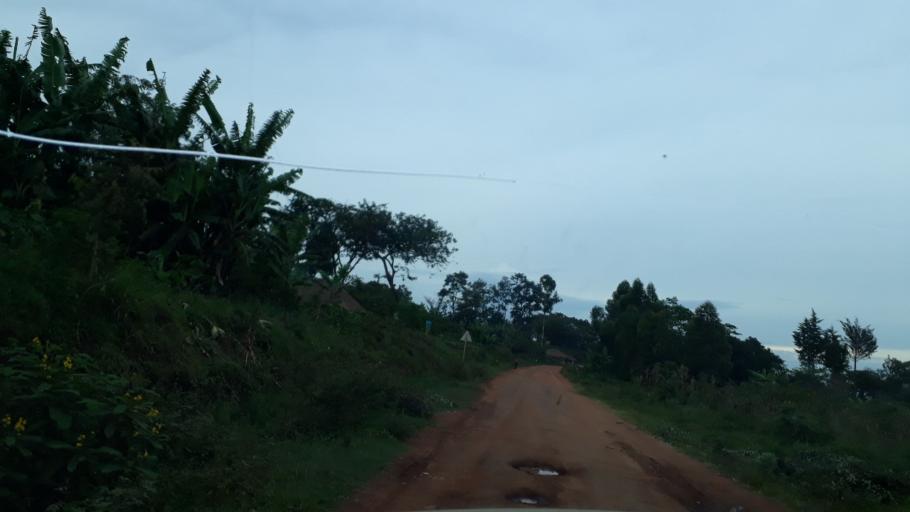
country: UG
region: Northern Region
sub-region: Zombo District
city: Paidha
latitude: 2.2050
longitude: 30.7412
